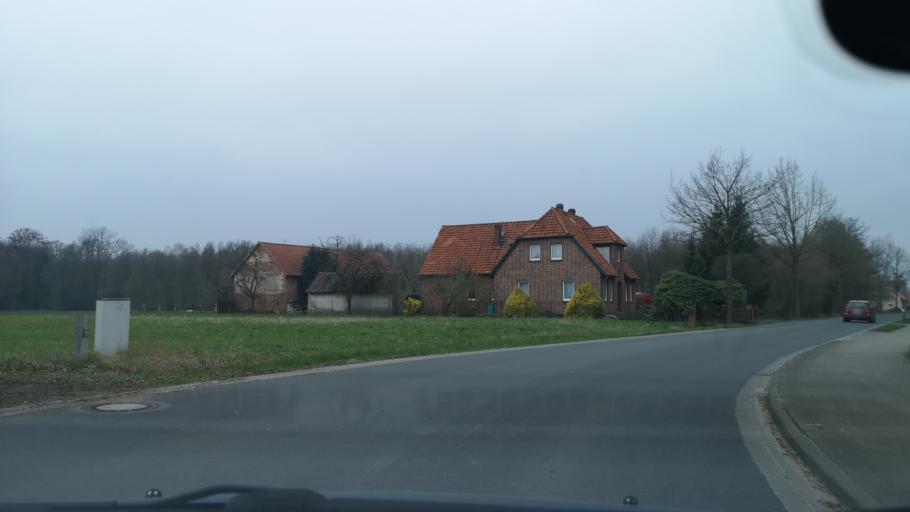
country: DE
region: Lower Saxony
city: Neustadt am Rubenberge
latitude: 52.4984
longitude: 9.5288
